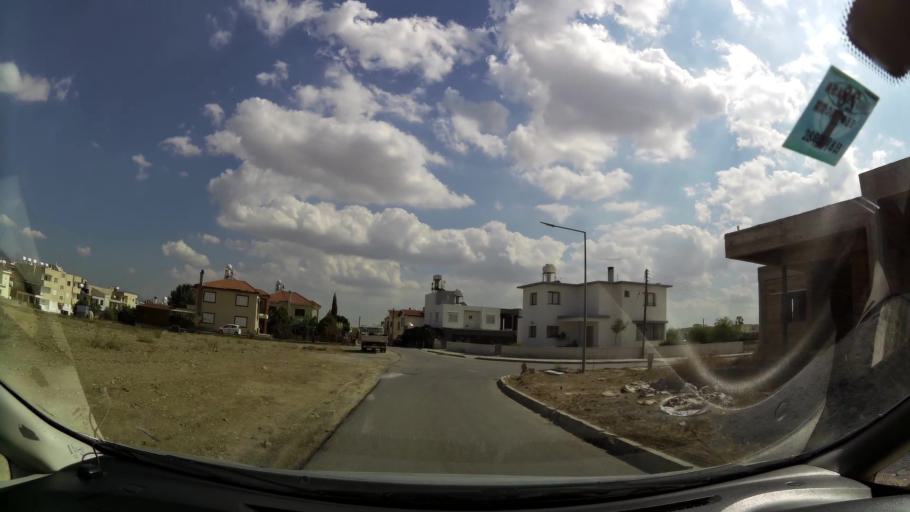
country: CY
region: Lefkosia
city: Nicosia
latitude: 35.2184
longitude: 33.2918
